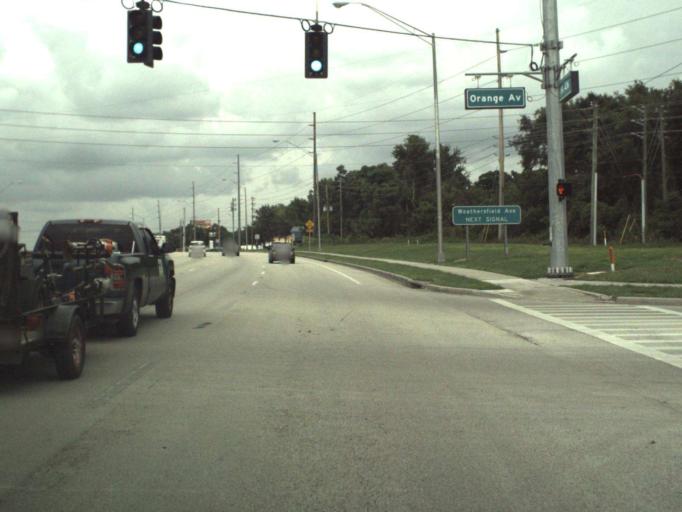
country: US
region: Florida
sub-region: Seminole County
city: Forest City
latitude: 28.6621
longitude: -81.4094
